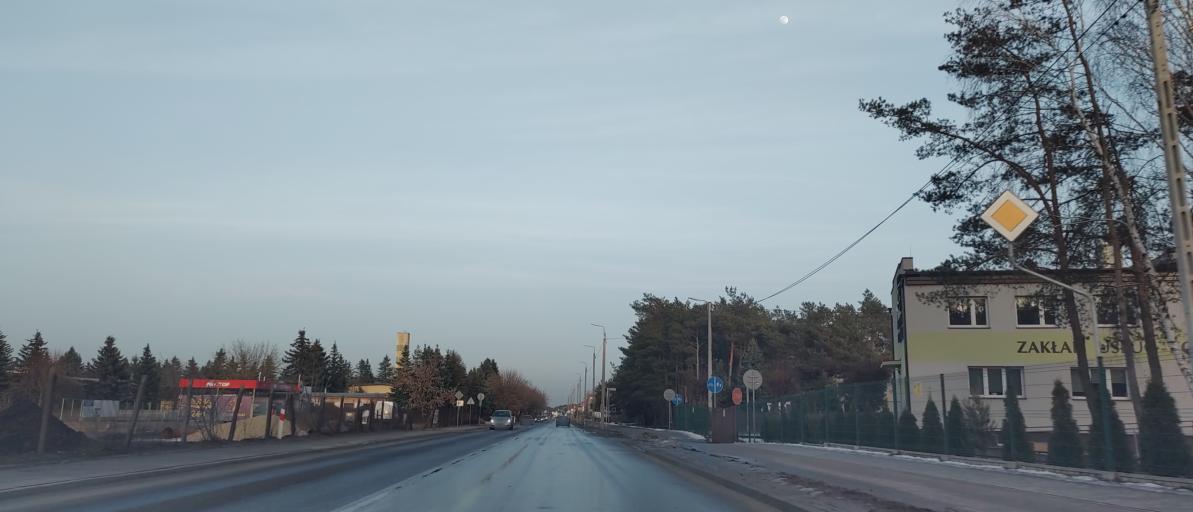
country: PL
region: Masovian Voivodeship
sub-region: Powiat bialobrzeski
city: Bialobrzegi
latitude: 51.6429
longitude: 20.9427
